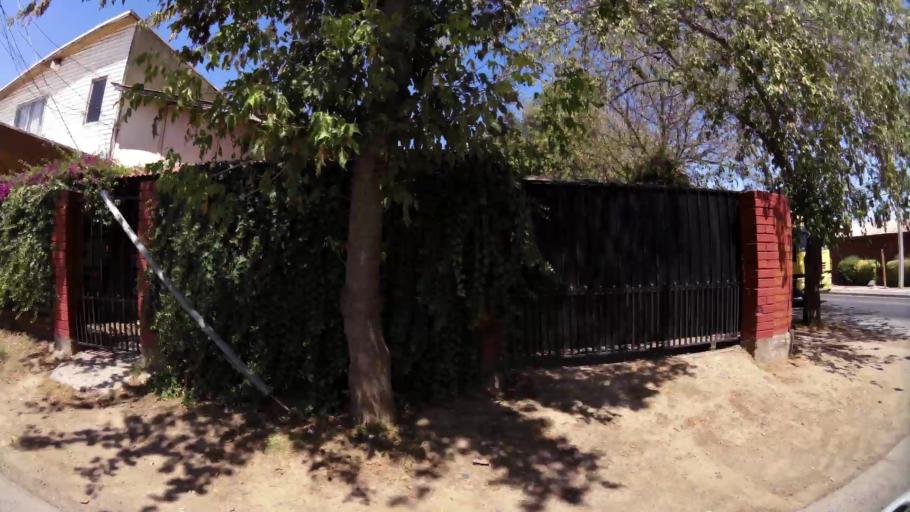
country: CL
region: Maule
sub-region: Provincia de Talca
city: Talca
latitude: -35.4311
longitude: -71.6335
